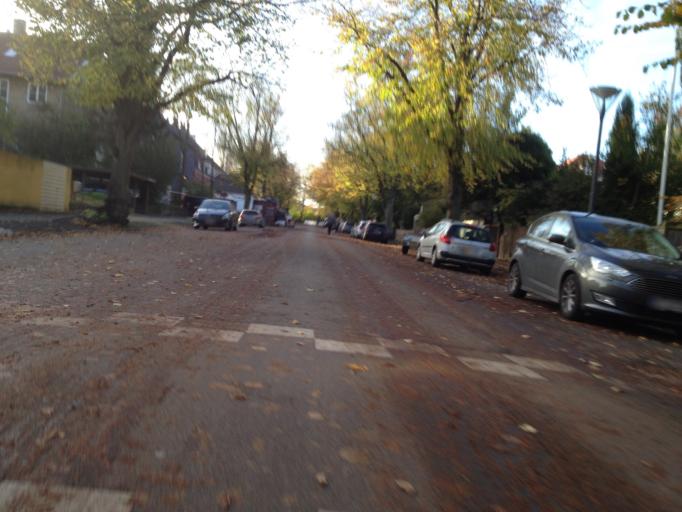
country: DK
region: Capital Region
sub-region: Gentofte Kommune
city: Charlottenlund
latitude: 55.7283
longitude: 12.5721
